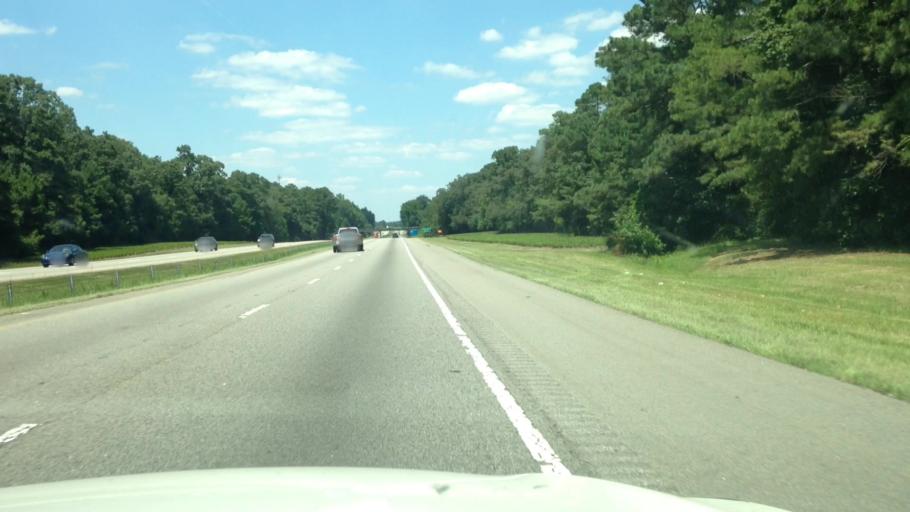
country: US
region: North Carolina
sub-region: Robeson County
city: Saint Pauls
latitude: 34.7950
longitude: -78.9931
